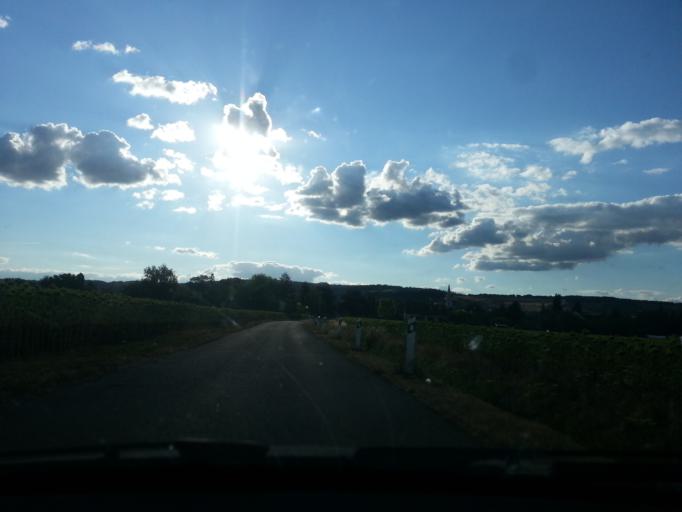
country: FR
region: Bourgogne
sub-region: Departement de Saone-et-Loire
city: Givry
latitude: 46.7783
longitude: 4.7545
